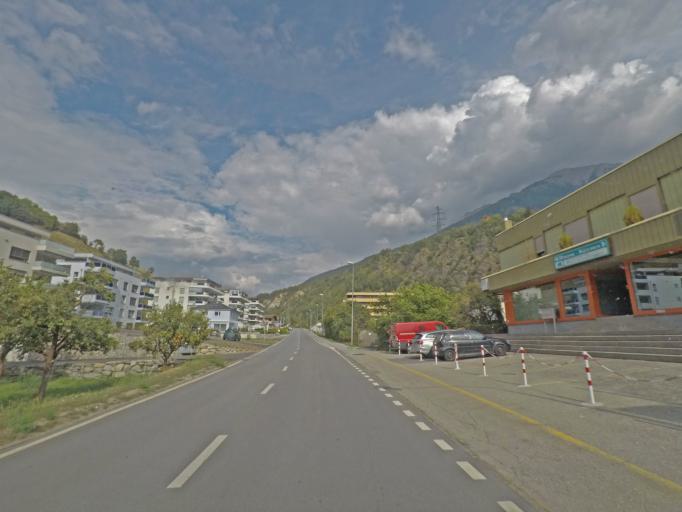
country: CH
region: Valais
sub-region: Brig District
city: Naters
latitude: 46.3270
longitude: 8.0080
